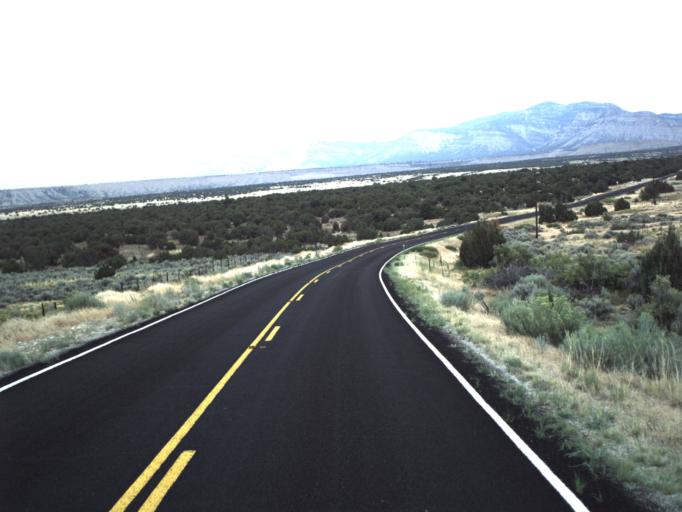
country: US
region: Utah
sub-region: Carbon County
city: East Carbon City
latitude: 39.4881
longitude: -110.4043
